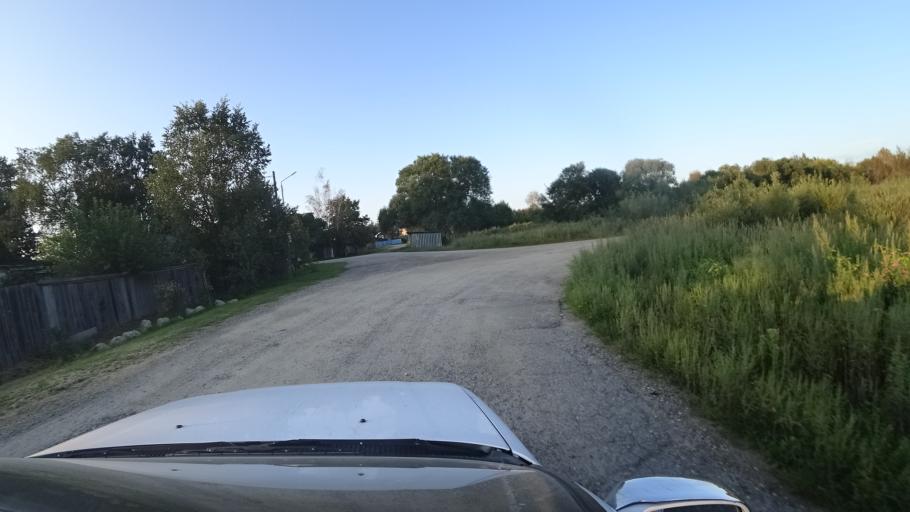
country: RU
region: Primorskiy
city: Dal'nerechensk
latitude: 45.9437
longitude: 133.7577
